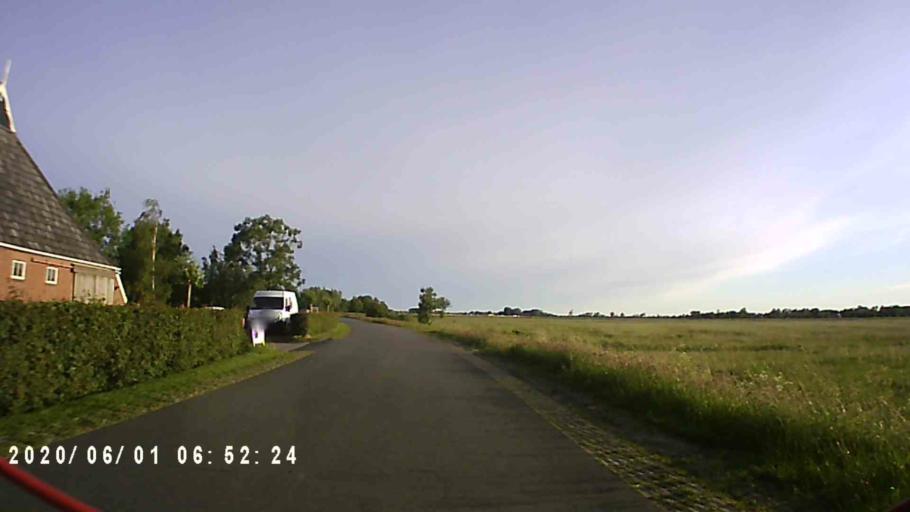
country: NL
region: Friesland
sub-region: Gemeente Kollumerland en Nieuwkruisland
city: Kollum
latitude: 53.3086
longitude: 6.1312
